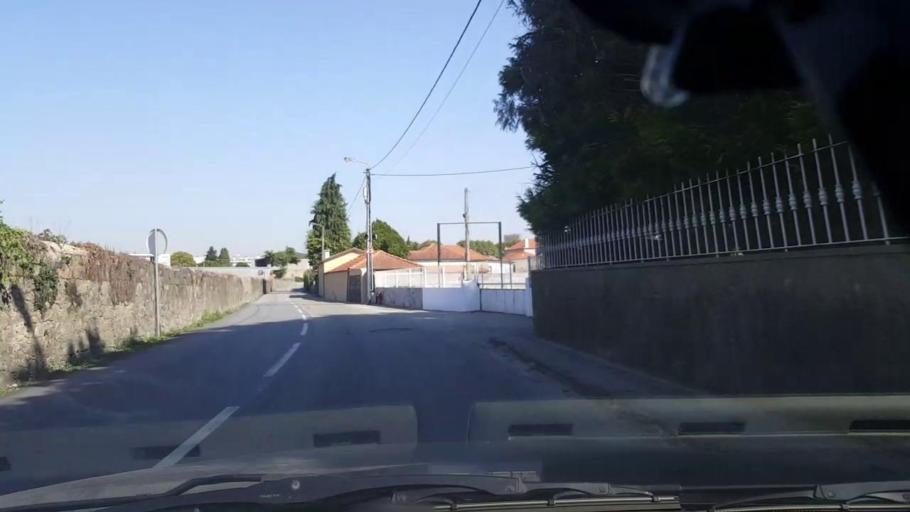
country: PT
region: Porto
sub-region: Vila do Conde
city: Arvore
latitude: 41.3357
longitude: -8.6822
